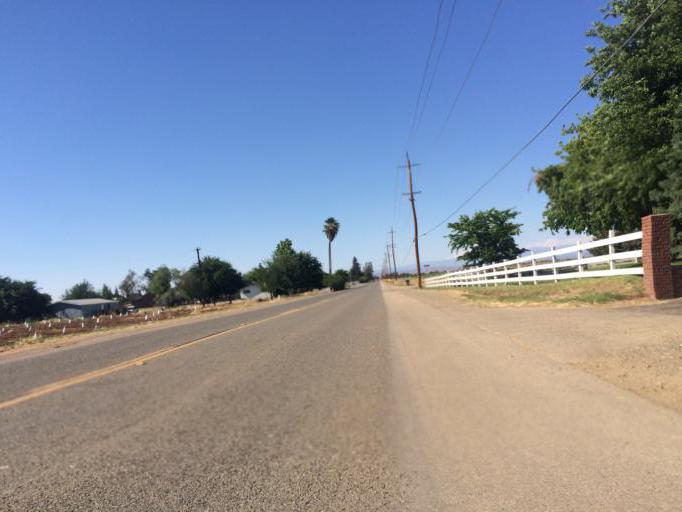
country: US
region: California
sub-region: Fresno County
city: Tarpey Village
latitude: 36.7858
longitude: -119.6102
